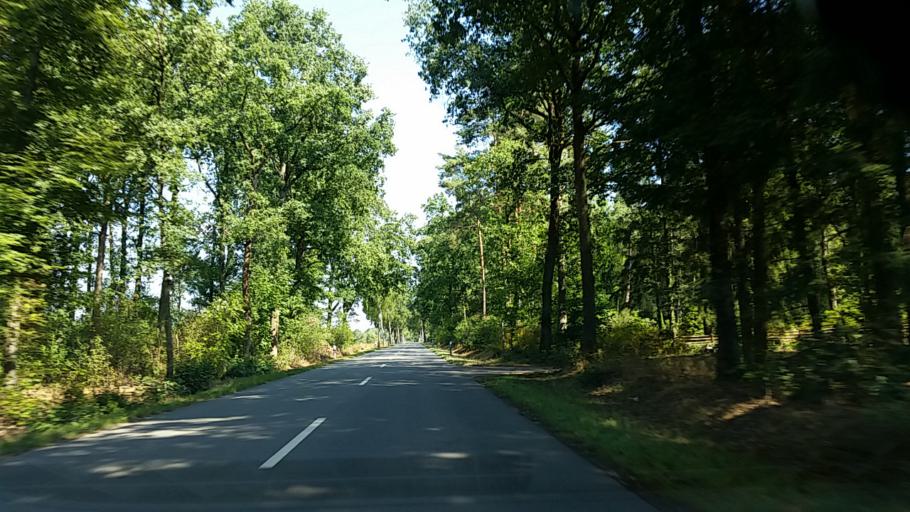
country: DE
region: Lower Saxony
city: Bienenbuttel
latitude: 53.1631
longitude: 10.5092
